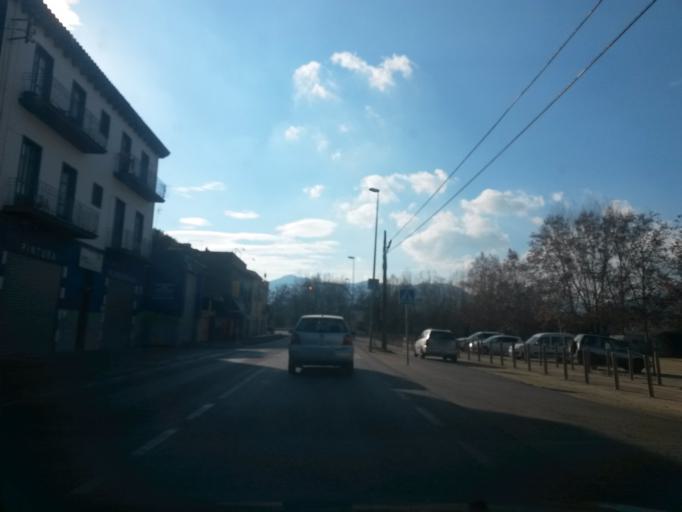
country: ES
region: Catalonia
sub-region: Provincia de Girona
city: Angles
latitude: 41.9705
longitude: 2.6741
